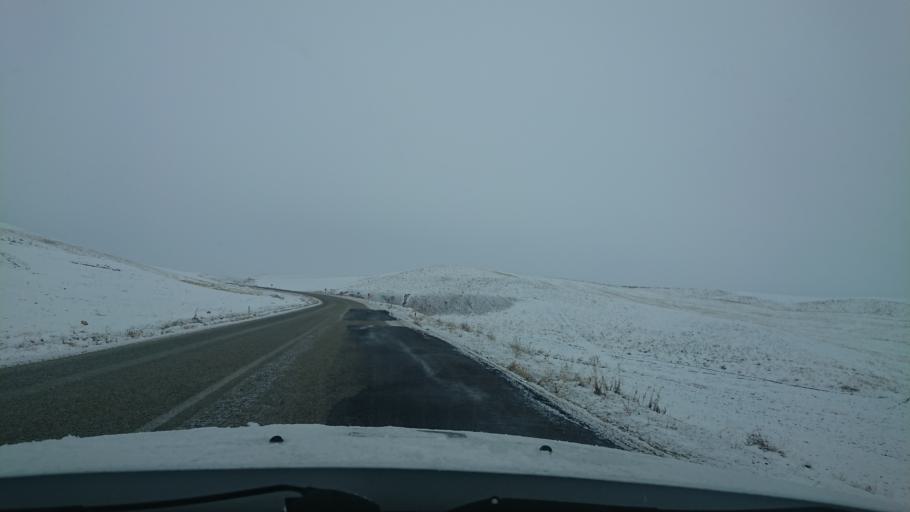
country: TR
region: Aksaray
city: Agacoren
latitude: 38.7678
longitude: 33.8706
